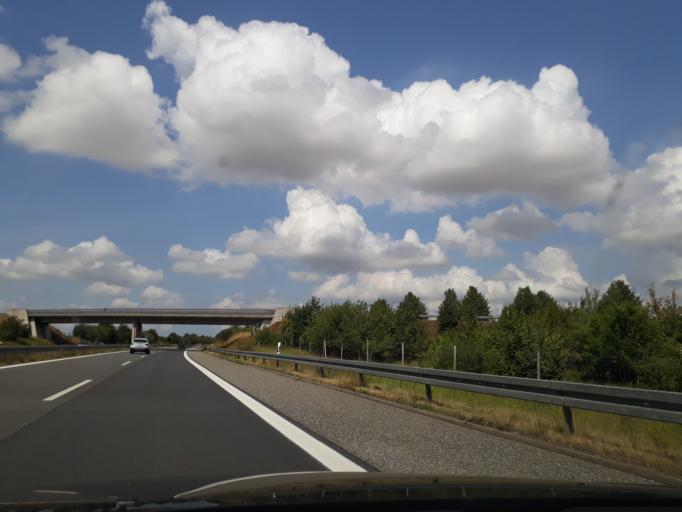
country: DE
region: Brandenburg
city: Grunow
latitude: 53.2736
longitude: 13.9922
